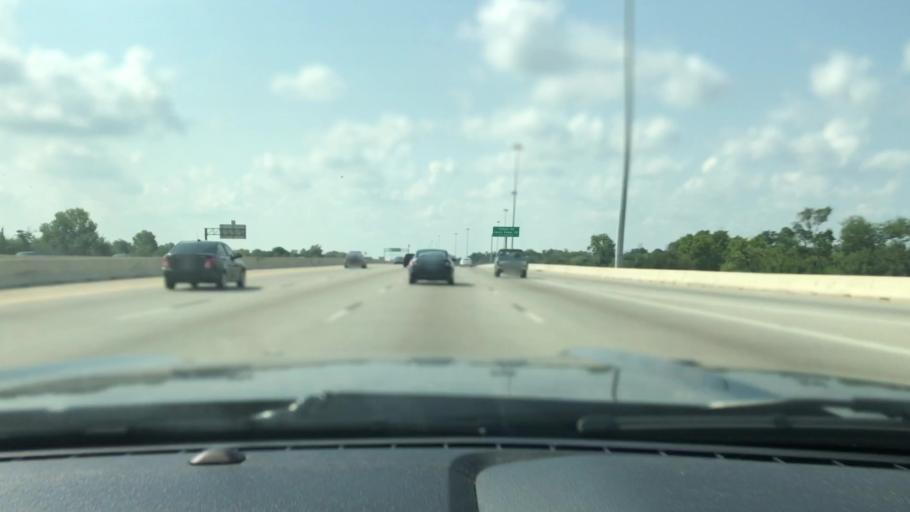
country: US
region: Texas
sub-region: Harris County
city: Aldine
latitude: 29.8618
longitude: -95.3337
